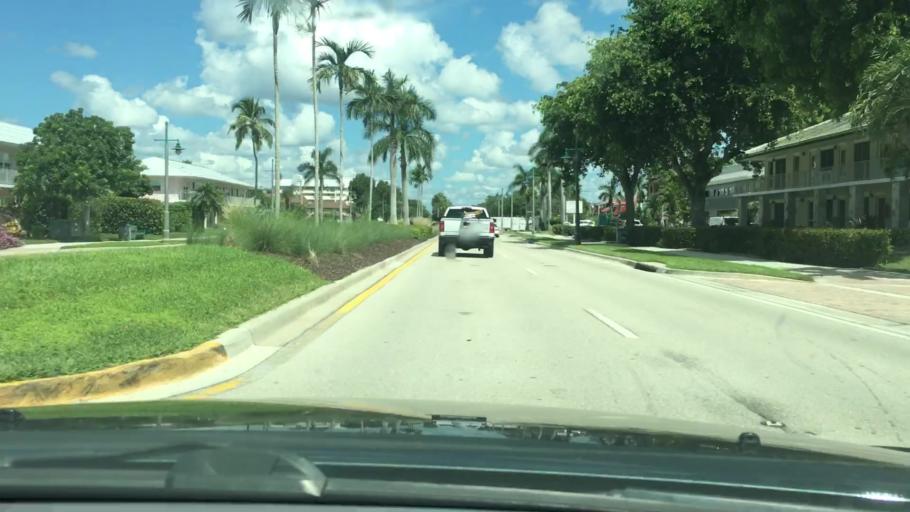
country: US
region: Florida
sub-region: Collier County
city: Marco
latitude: 25.9407
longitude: -81.7326
